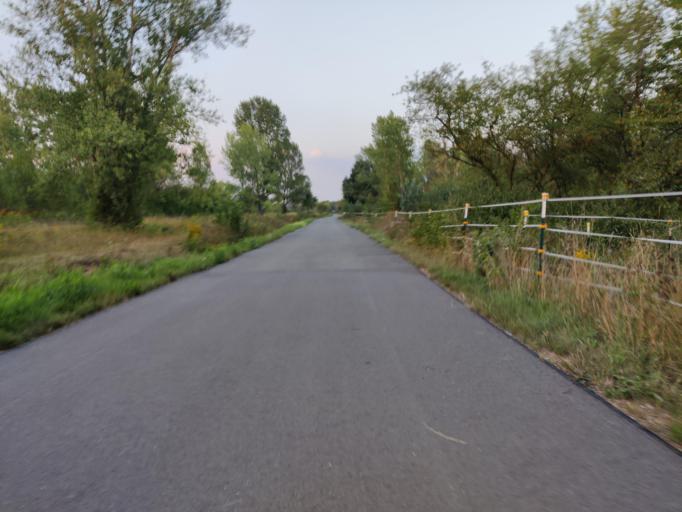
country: DE
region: Saxony
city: Zschortau
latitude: 51.4476
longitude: 12.3227
